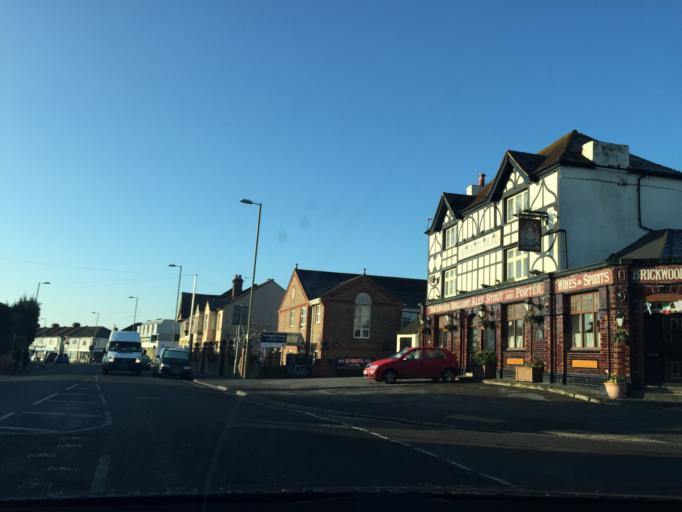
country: GB
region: England
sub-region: Hampshire
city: Gosport
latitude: 50.8060
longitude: -1.1526
